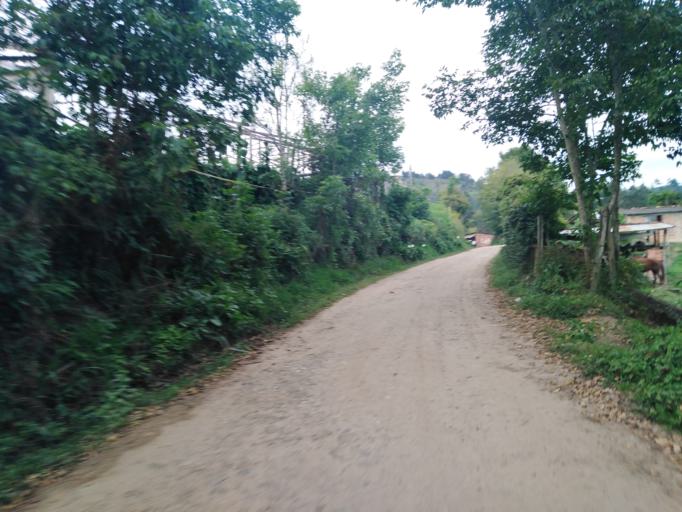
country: CO
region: Cundinamarca
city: Tenza
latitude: 5.1147
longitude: -73.4093
